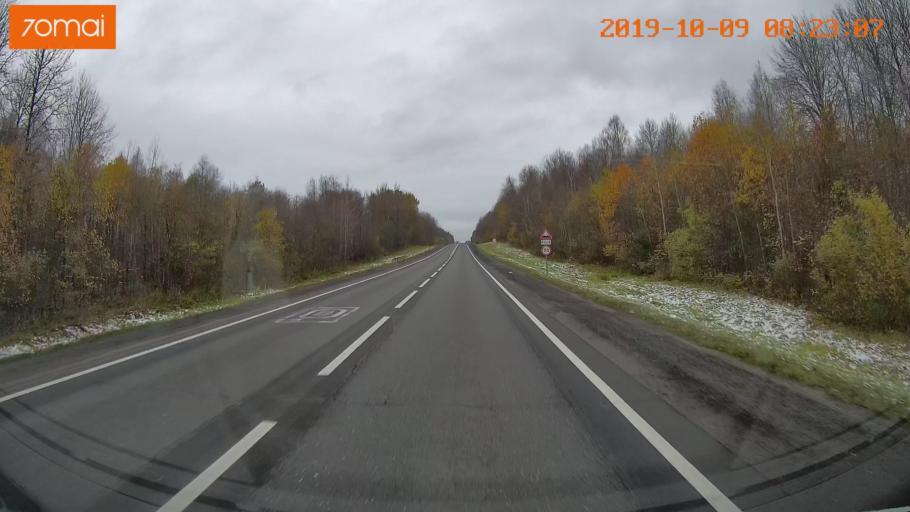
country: RU
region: Vologda
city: Gryazovets
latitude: 58.7504
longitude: 40.2850
